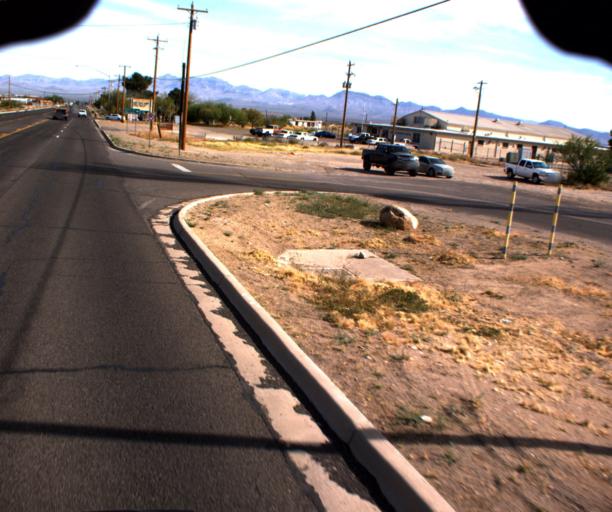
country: US
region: Arizona
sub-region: Graham County
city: Cactus Flat
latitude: 32.7938
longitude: -109.7077
